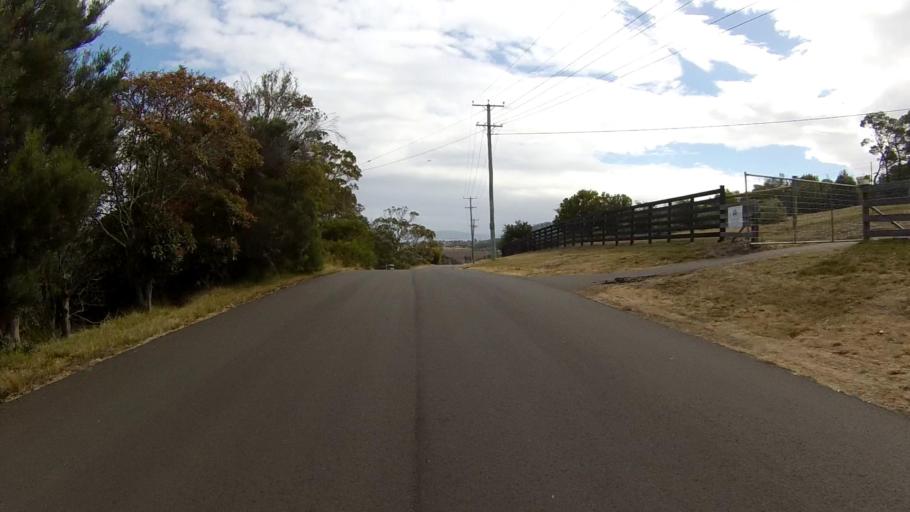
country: AU
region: Tasmania
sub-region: Clarence
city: Acton Park
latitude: -42.8840
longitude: 147.5027
